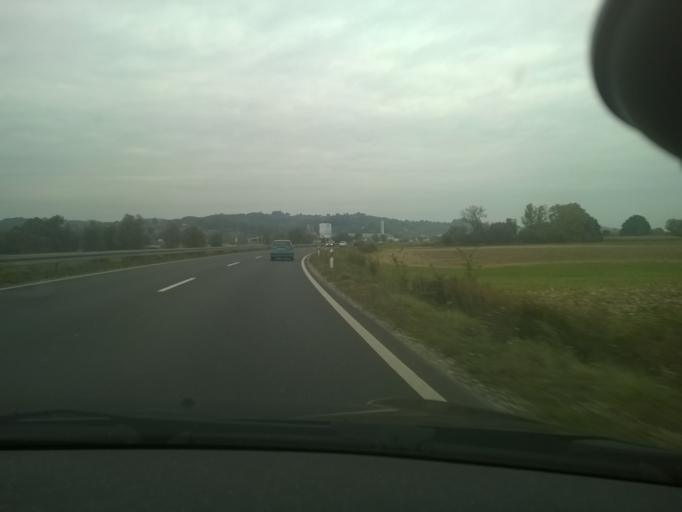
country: HR
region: Zagrebacka
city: Pojatno
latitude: 45.9025
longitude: 15.8135
